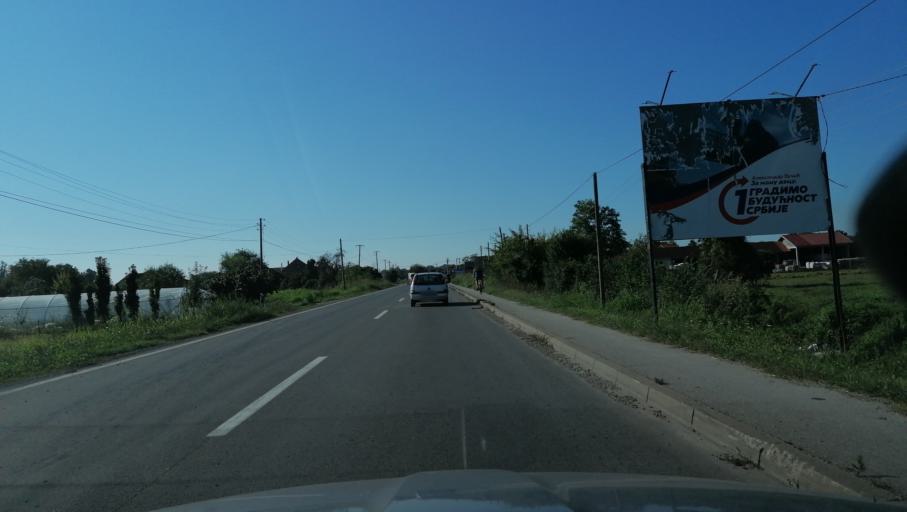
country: RS
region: Central Serbia
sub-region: Raski Okrug
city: Kraljevo
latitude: 43.7599
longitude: 20.6503
